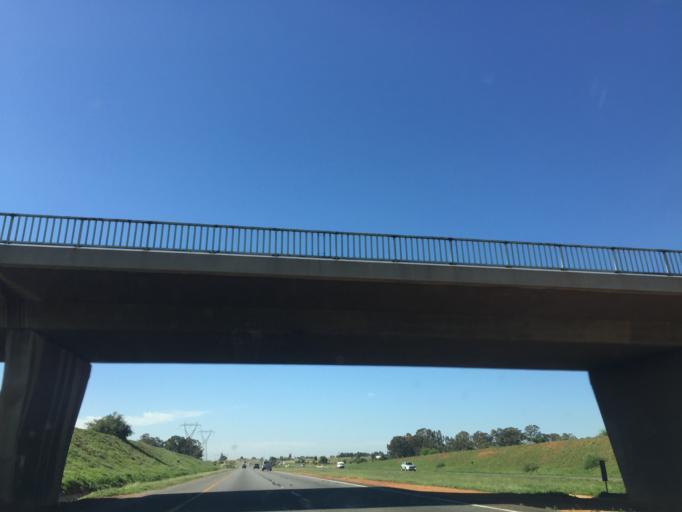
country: ZA
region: Gauteng
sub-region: Sedibeng District Municipality
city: Meyerton
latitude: -26.4518
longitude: 28.0720
